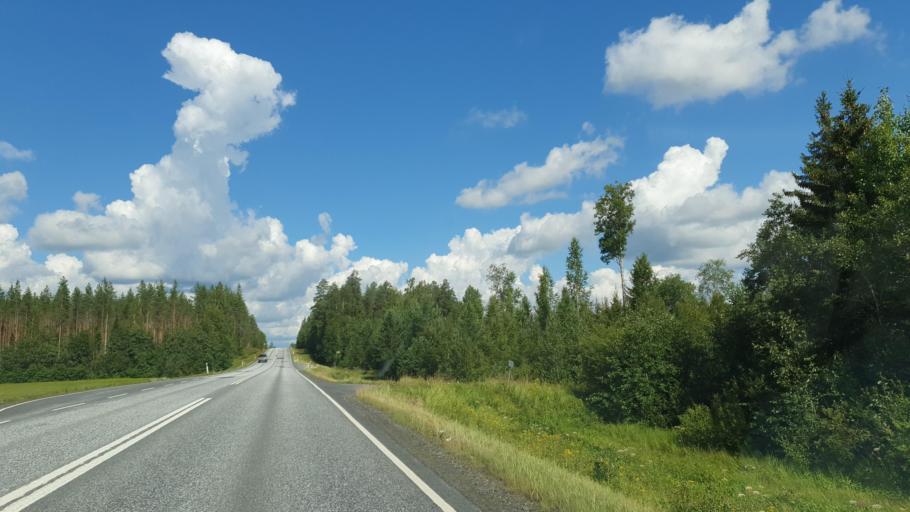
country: FI
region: Northern Savo
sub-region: Ylae-Savo
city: Sonkajaervi
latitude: 63.8194
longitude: 27.4209
